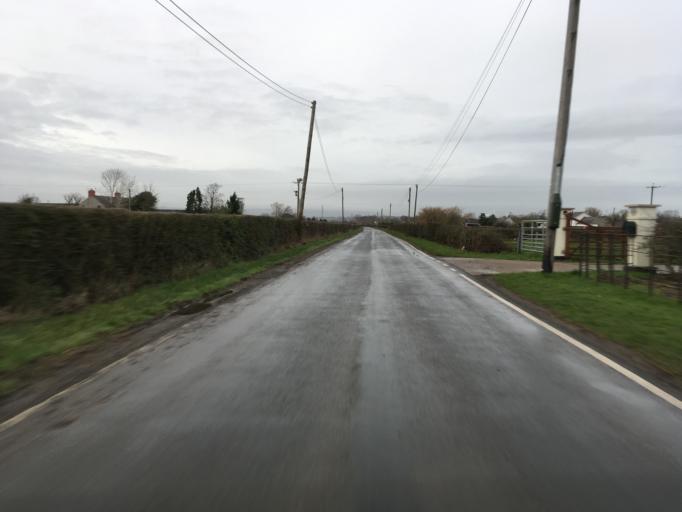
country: GB
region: Wales
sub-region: Newport
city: Goldcliff
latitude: 51.5490
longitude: -2.9007
